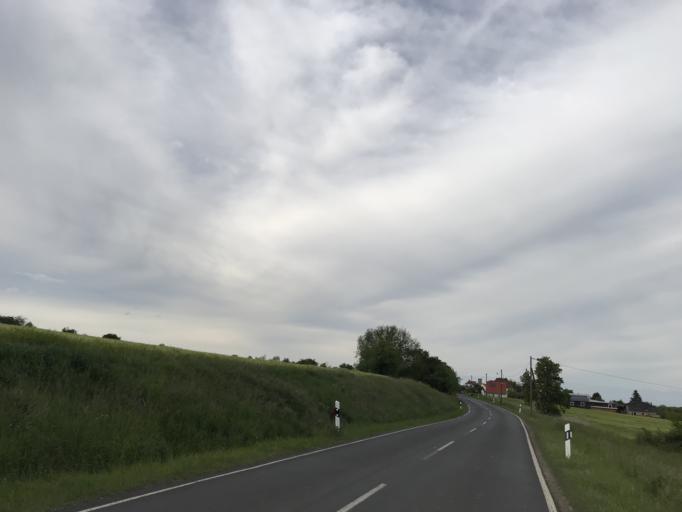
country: DE
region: Hesse
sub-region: Regierungsbezirk Giessen
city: Hoernsheim
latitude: 50.5056
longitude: 8.6135
